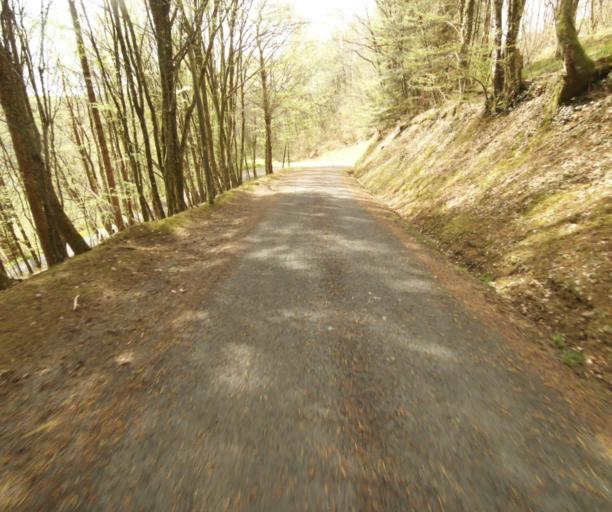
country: FR
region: Limousin
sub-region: Departement de la Correze
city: Laguenne
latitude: 45.2523
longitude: 1.8182
